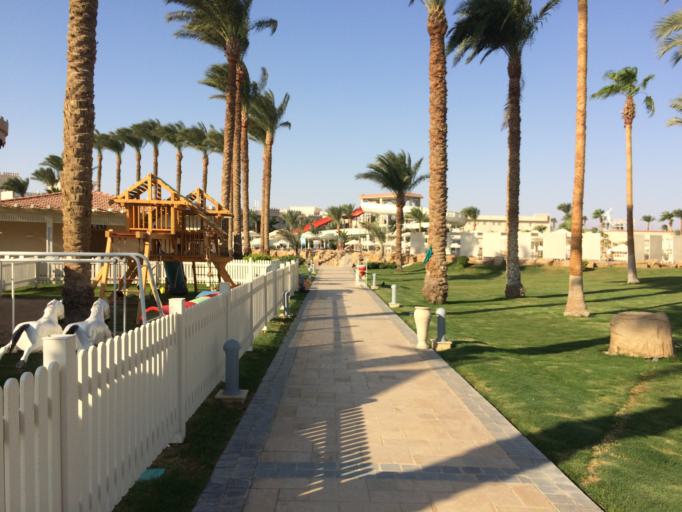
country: EG
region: Red Sea
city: Hurghada
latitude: 27.1224
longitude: 33.8267
